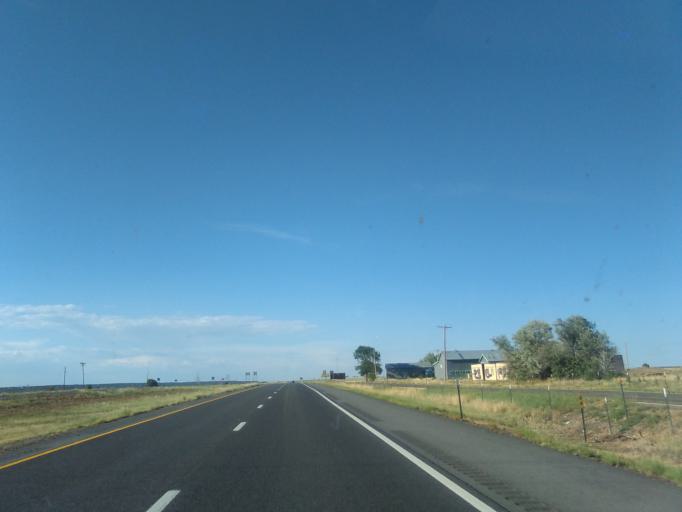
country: US
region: New Mexico
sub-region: San Miguel County
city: Las Vegas
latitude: 35.6560
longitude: -105.1892
